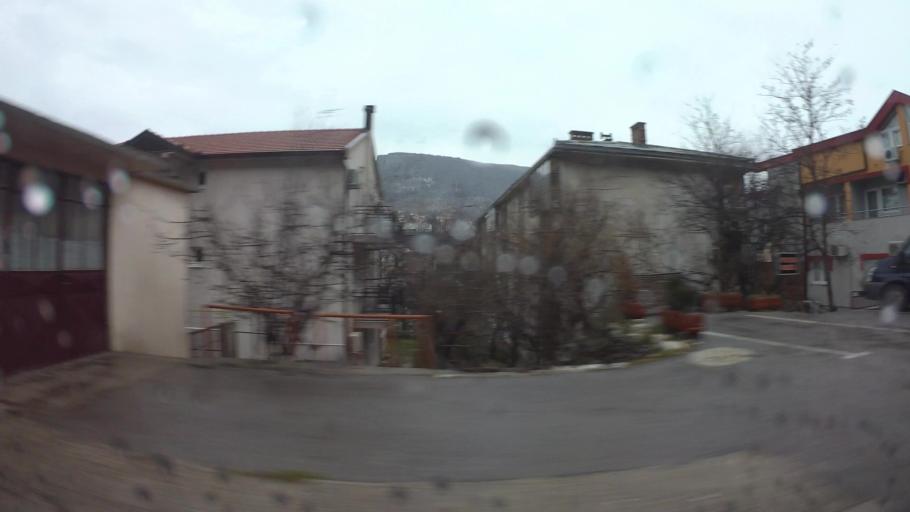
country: BA
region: Federation of Bosnia and Herzegovina
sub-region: Hercegovacko-Bosanski Kanton
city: Mostar
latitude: 43.3326
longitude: 17.8147
